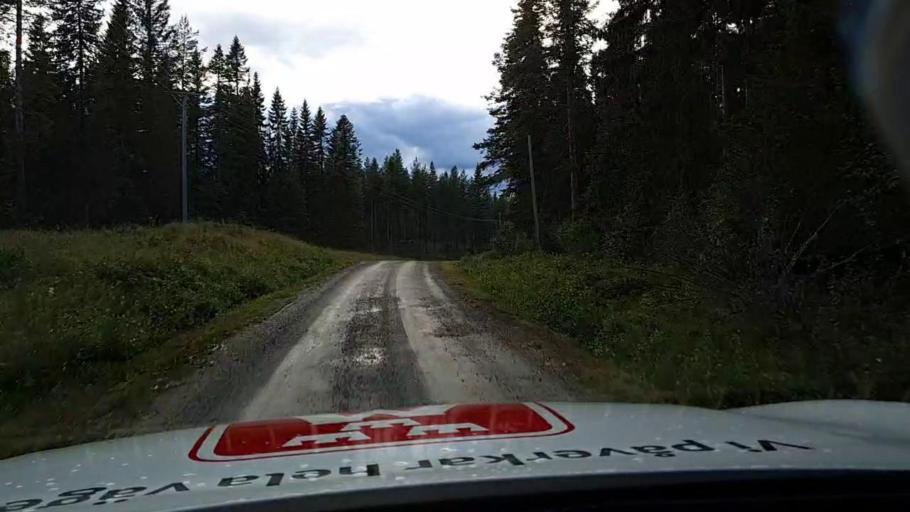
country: SE
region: Jaemtland
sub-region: Bergs Kommun
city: Hoverberg
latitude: 62.8802
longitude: 14.5977
